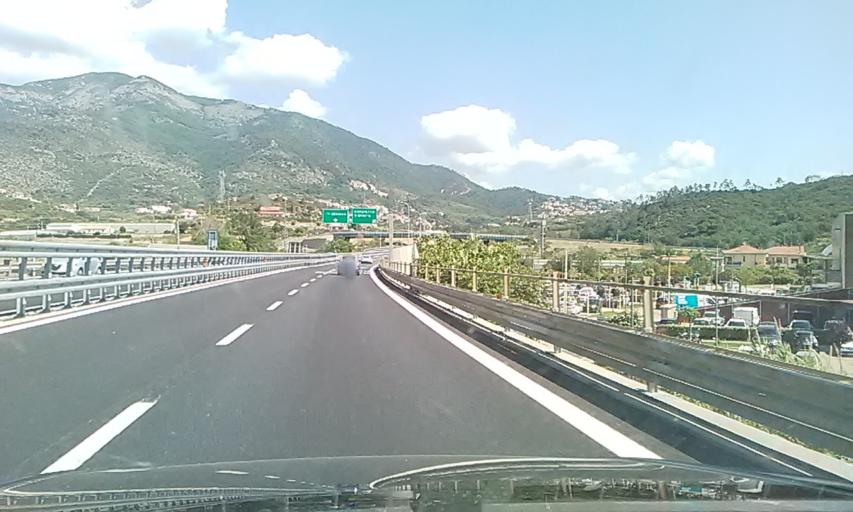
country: IT
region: Liguria
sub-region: Provincia di Savona
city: Boissano
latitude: 44.1201
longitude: 8.2253
